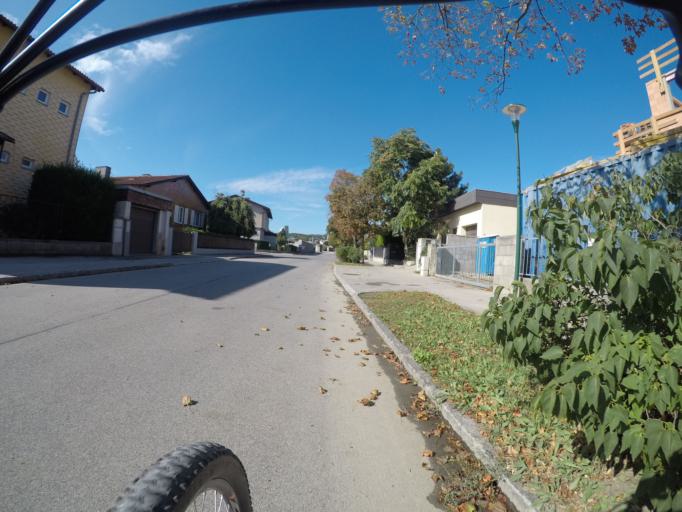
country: AT
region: Lower Austria
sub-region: Politischer Bezirk Modling
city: Brunn am Gebirge
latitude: 48.1075
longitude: 16.2941
